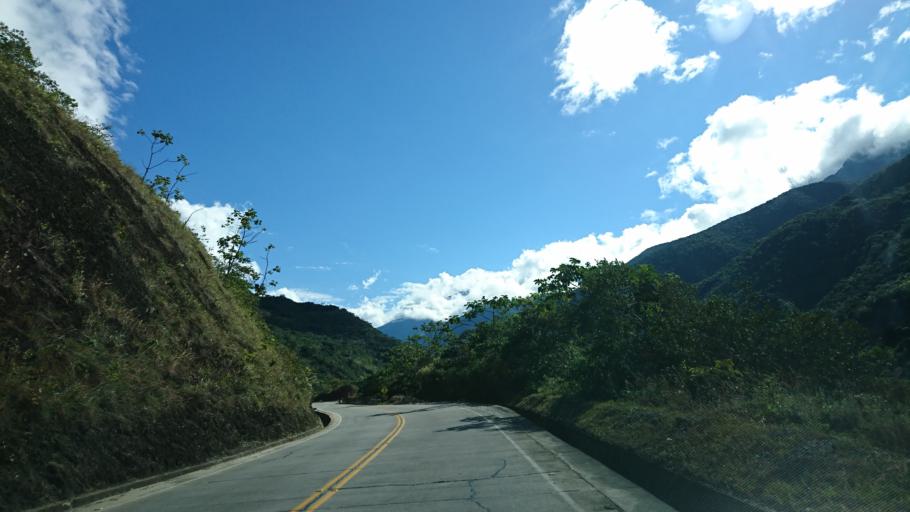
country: BO
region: La Paz
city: Coroico
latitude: -16.2019
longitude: -67.7645
